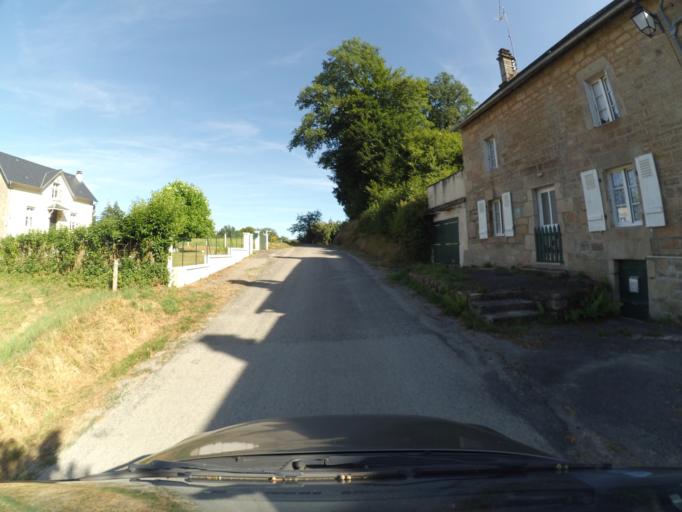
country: FR
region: Limousin
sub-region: Departement de la Correze
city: Bugeat
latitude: 45.6893
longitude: 1.8881
